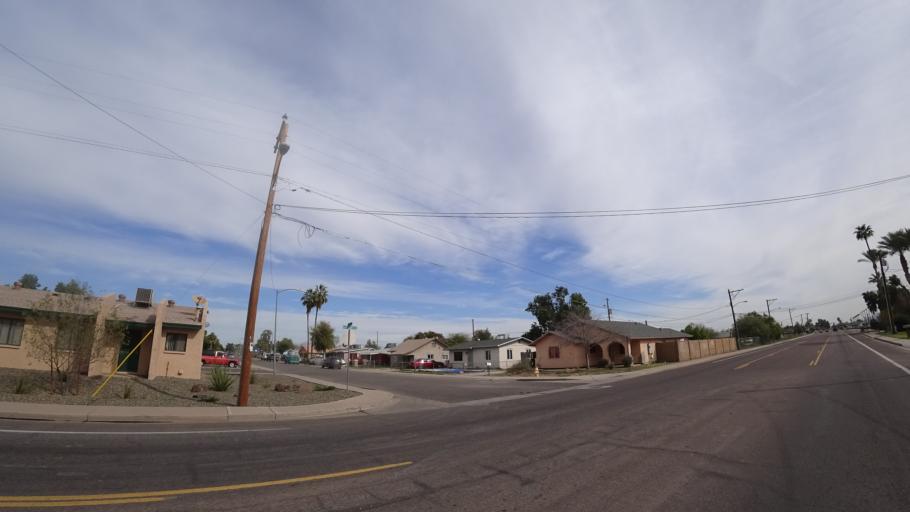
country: US
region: Arizona
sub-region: Maricopa County
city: Glendale
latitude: 33.5312
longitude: -112.1727
